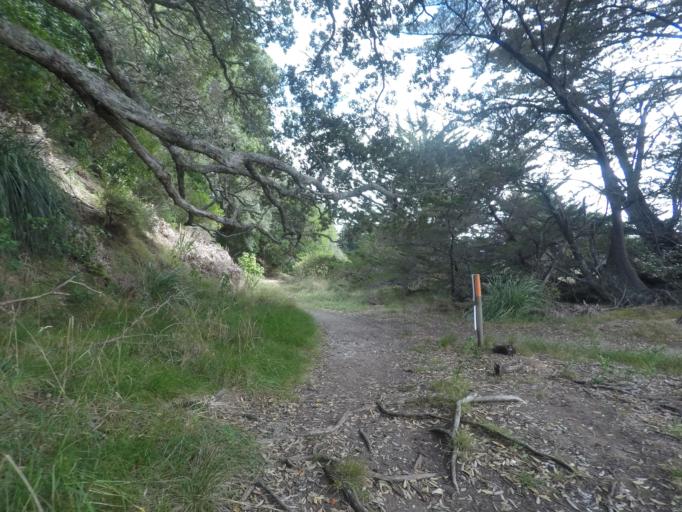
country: NZ
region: Auckland
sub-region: Auckland
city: Rothesay Bay
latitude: -36.6457
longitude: 174.7252
